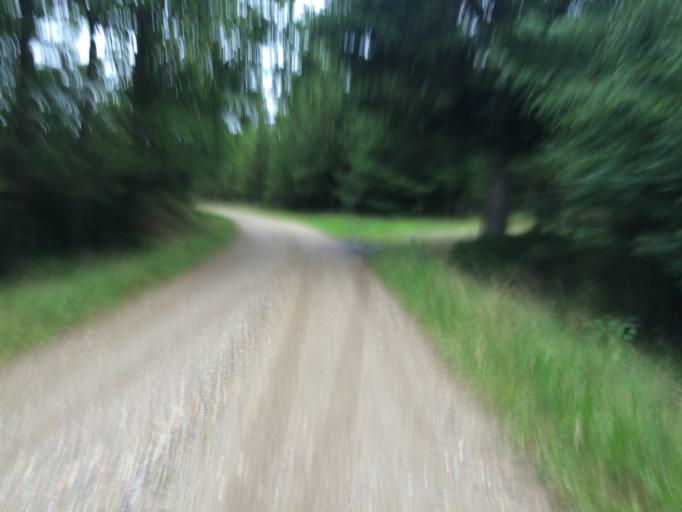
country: DK
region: Central Jutland
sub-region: Holstebro Kommune
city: Ulfborg
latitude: 56.2283
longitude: 8.4131
